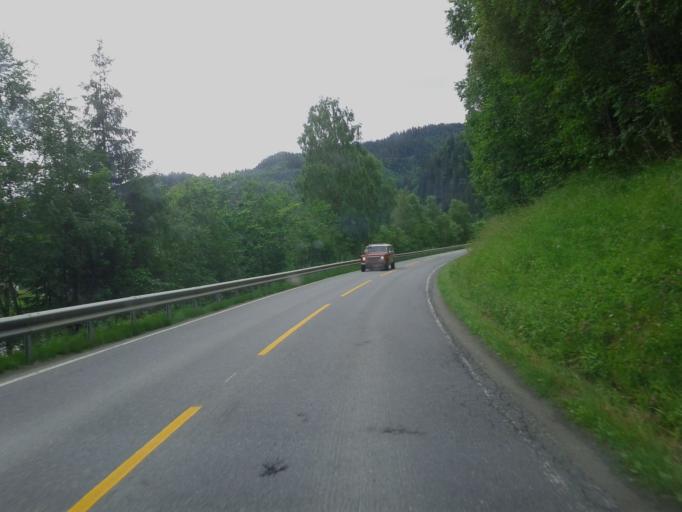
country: NO
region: Sor-Trondelag
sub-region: Midtre Gauldal
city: Storen
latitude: 62.9994
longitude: 10.4643
